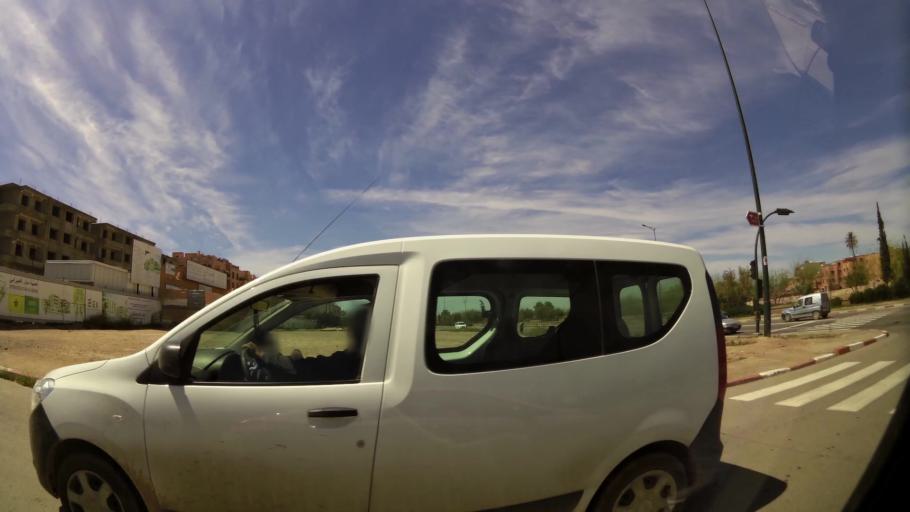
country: MA
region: Marrakech-Tensift-Al Haouz
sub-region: Marrakech
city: Marrakesh
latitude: 31.6622
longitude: -7.9872
